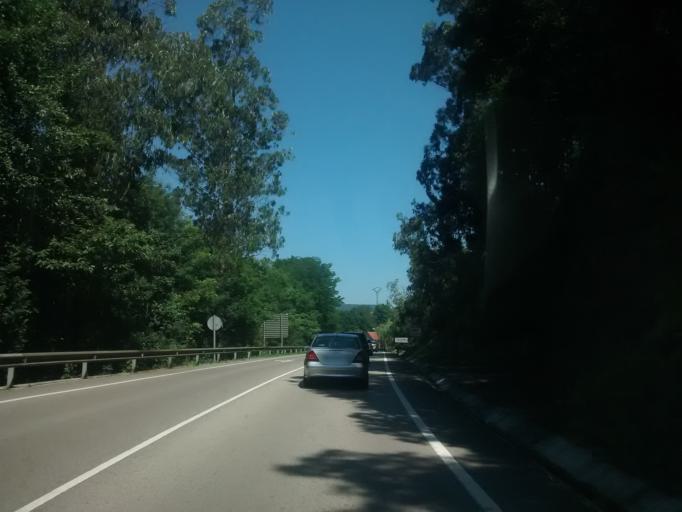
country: ES
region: Cantabria
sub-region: Provincia de Cantabria
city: San Miguel de Meruelo
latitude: 43.4338
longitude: -3.5693
